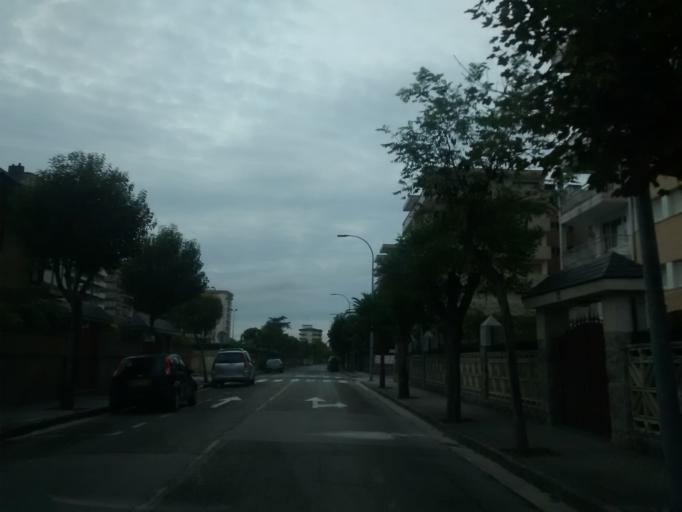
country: ES
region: Cantabria
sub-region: Provincia de Cantabria
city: Laredo
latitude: 43.4119
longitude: -3.4338
